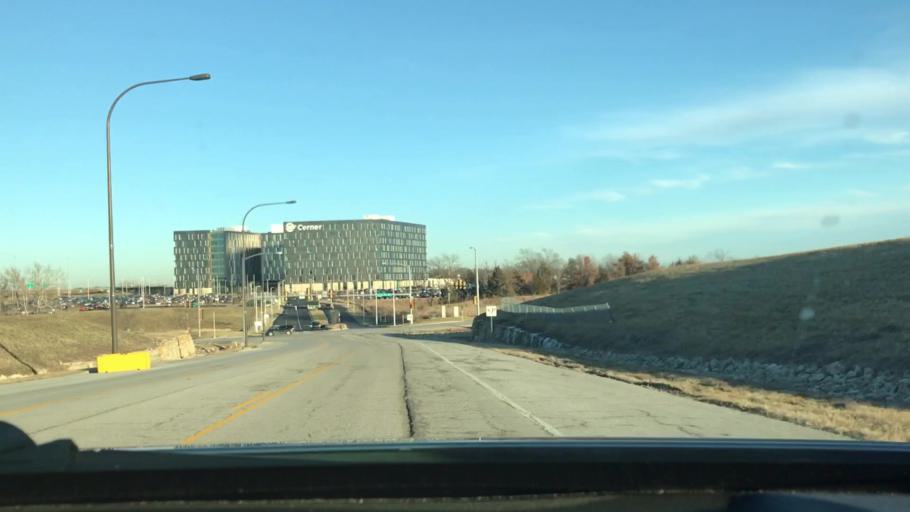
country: US
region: Kansas
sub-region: Wyandotte County
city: Edwardsville
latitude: 39.1138
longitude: -94.8217
